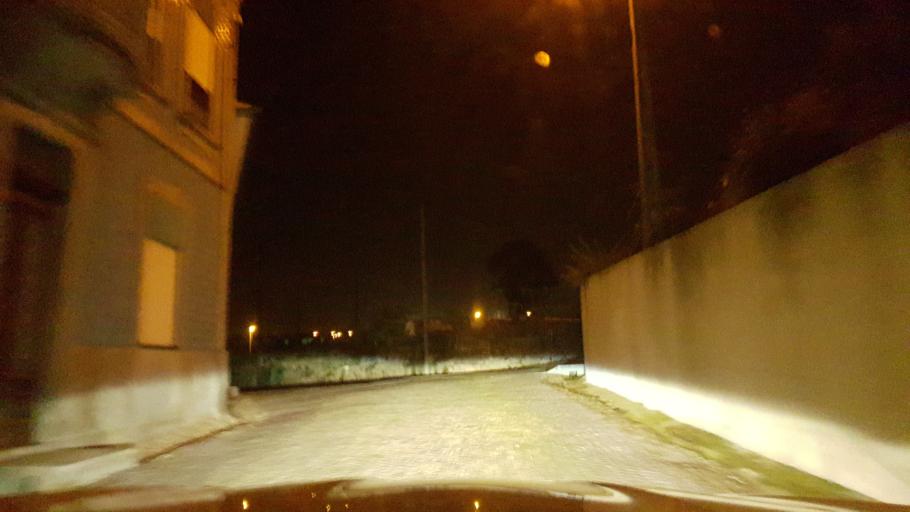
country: PT
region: Porto
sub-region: Matosinhos
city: Guifoes
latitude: 41.2151
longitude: -8.6476
